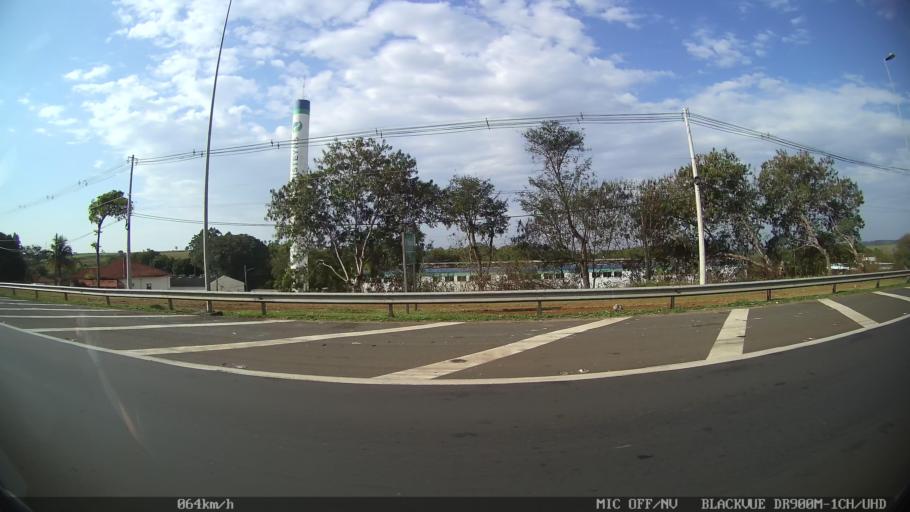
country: BR
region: Sao Paulo
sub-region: Cosmopolis
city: Cosmopolis
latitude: -22.6883
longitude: -47.1561
